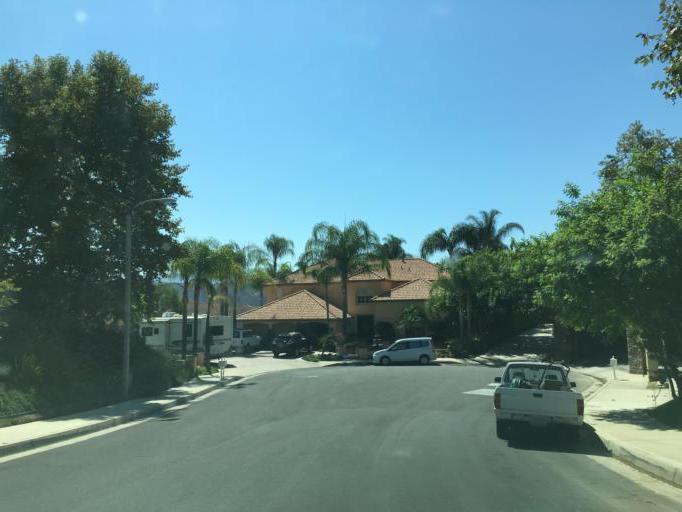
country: US
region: California
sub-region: Los Angeles County
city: Agoura
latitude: 34.1301
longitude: -118.7164
